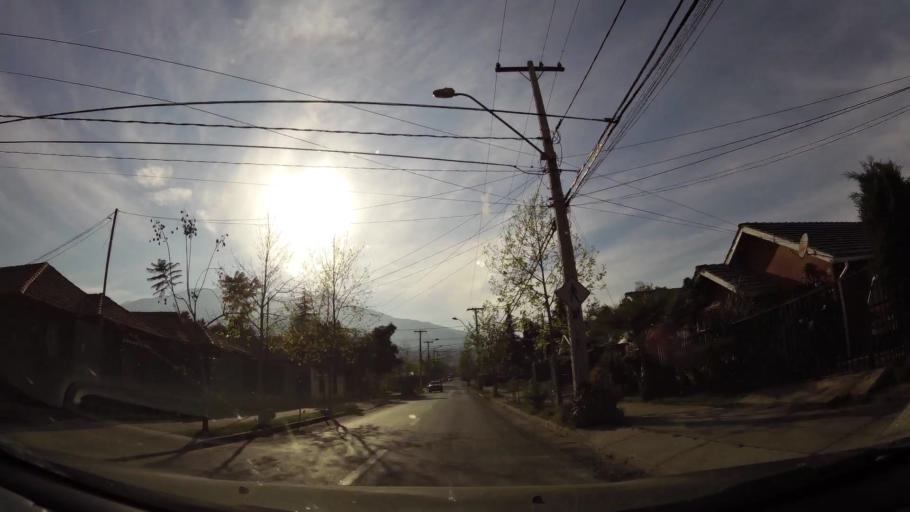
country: CL
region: Santiago Metropolitan
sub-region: Provincia de Cordillera
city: Puente Alto
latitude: -33.5700
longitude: -70.5488
